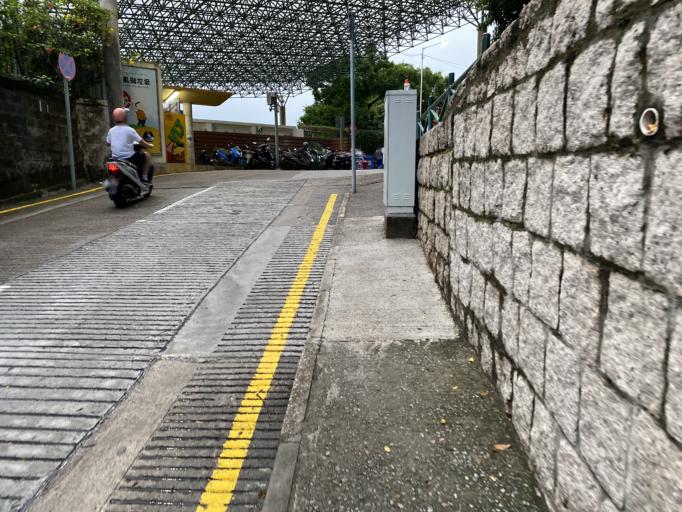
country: MO
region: Macau
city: Macau
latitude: 22.1967
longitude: 113.5488
